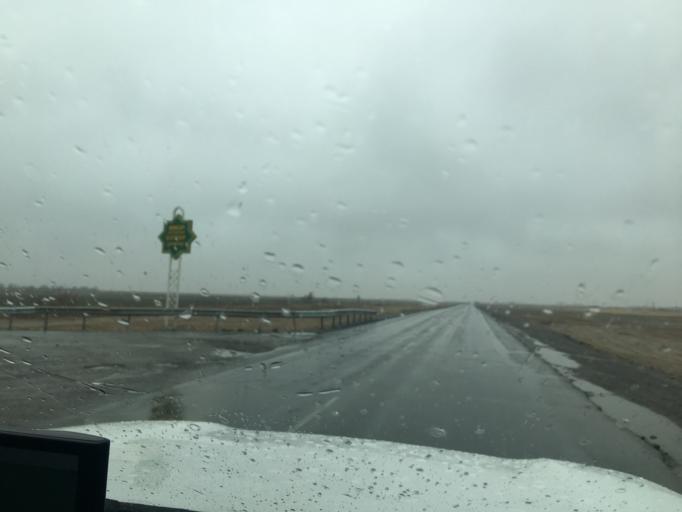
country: TM
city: Murgab
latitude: 37.4559
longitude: 62.0618
